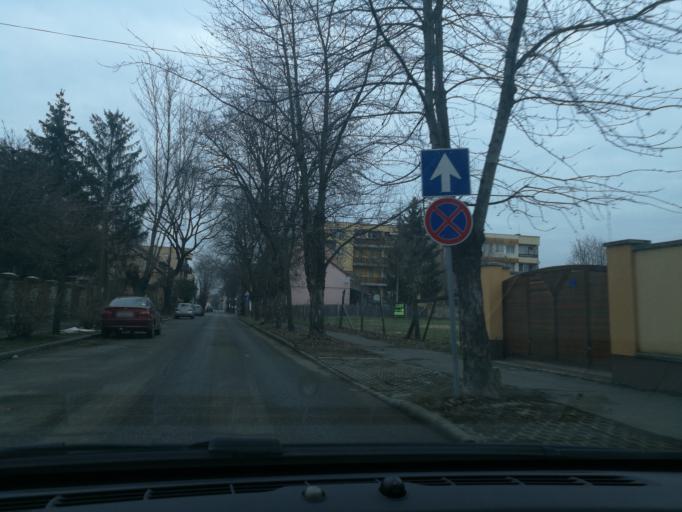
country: HU
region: Szabolcs-Szatmar-Bereg
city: Nyiregyhaza
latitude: 47.9500
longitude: 21.7107
